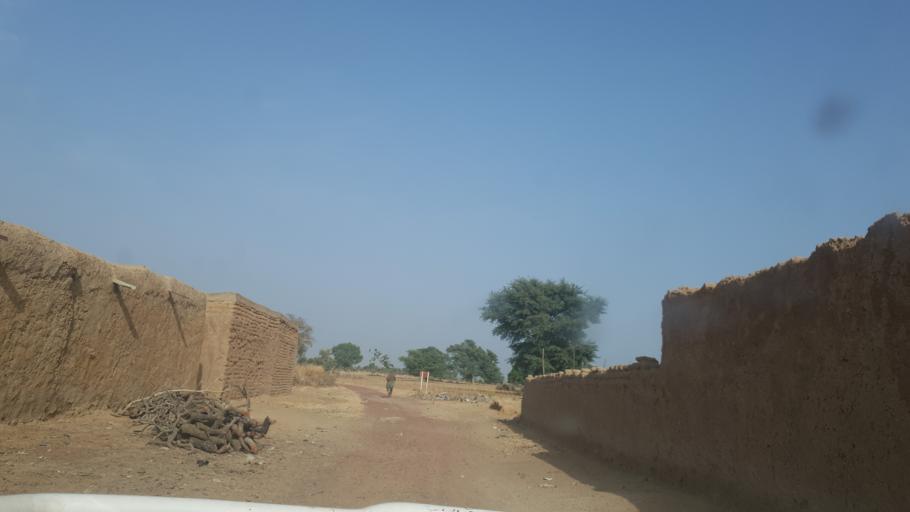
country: ML
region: Segou
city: Baroueli
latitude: 13.3538
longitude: -6.9293
